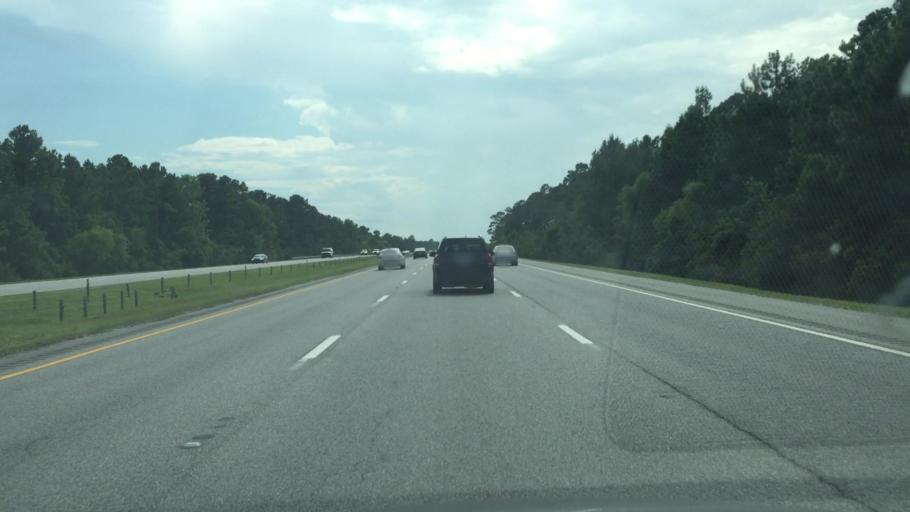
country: US
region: South Carolina
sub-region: Horry County
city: Myrtle Beach
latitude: 33.7785
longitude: -78.8116
